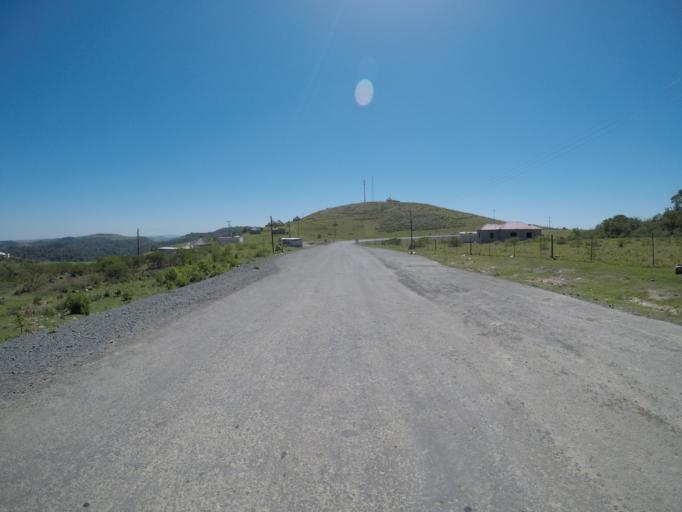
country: ZA
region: Eastern Cape
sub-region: OR Tambo District Municipality
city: Libode
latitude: -32.0017
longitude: 29.1166
